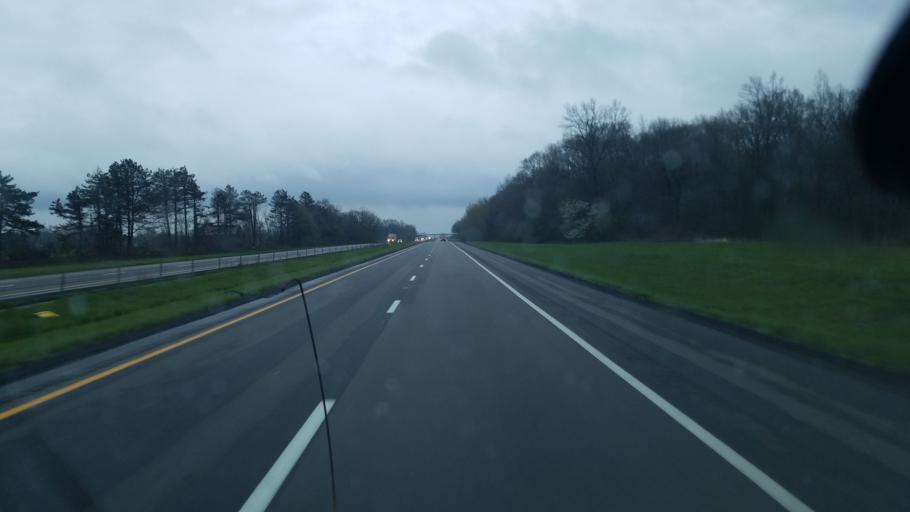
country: US
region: Ohio
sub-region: Medina County
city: Seville
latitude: 41.0318
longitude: -81.8220
